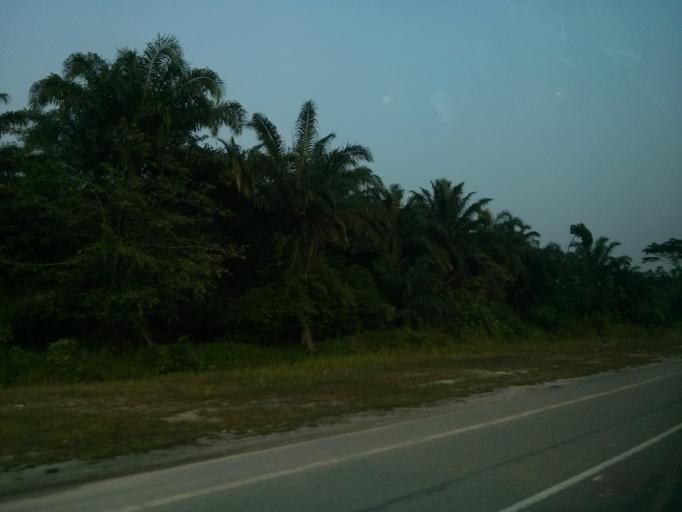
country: MY
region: Negeri Sembilan
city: Kampung Baharu Nilai
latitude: 2.8109
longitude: 101.6950
